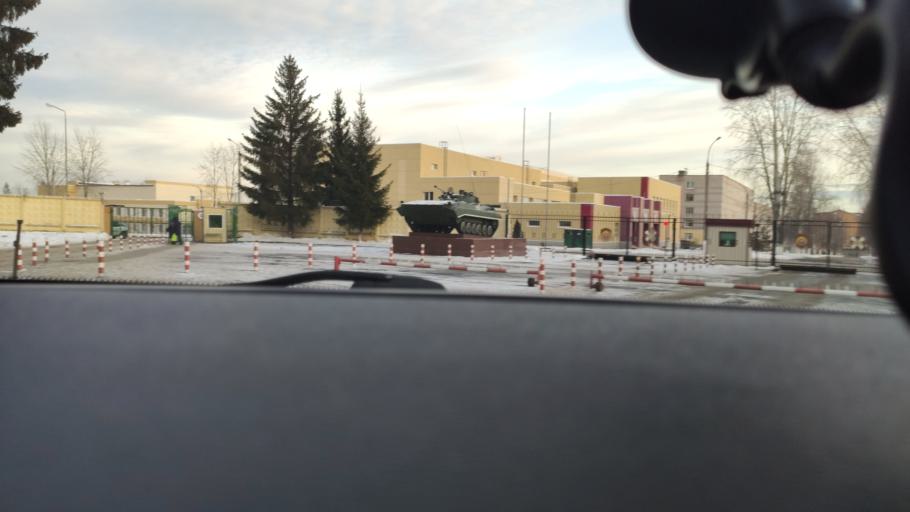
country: RU
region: Perm
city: Perm
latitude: 58.1215
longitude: 56.3041
